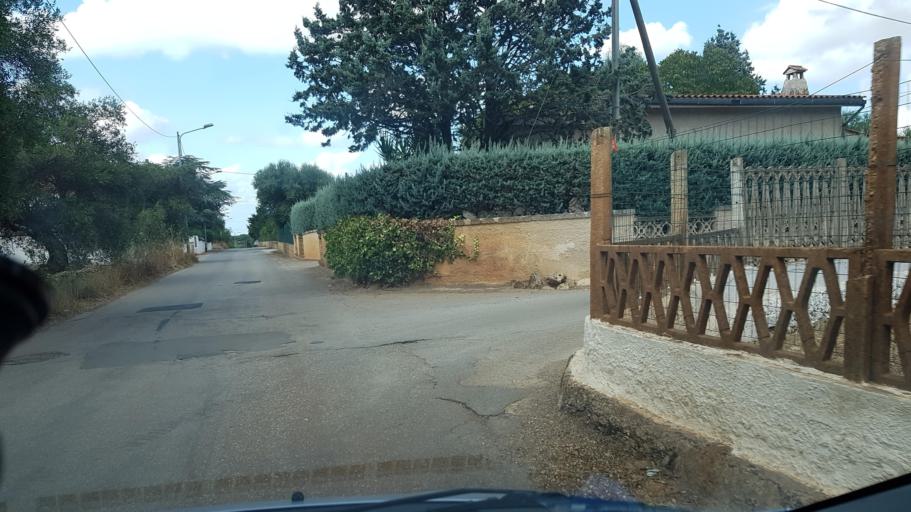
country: IT
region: Apulia
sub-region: Provincia di Brindisi
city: San Vito dei Normanni
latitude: 40.6633
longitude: 17.7163
